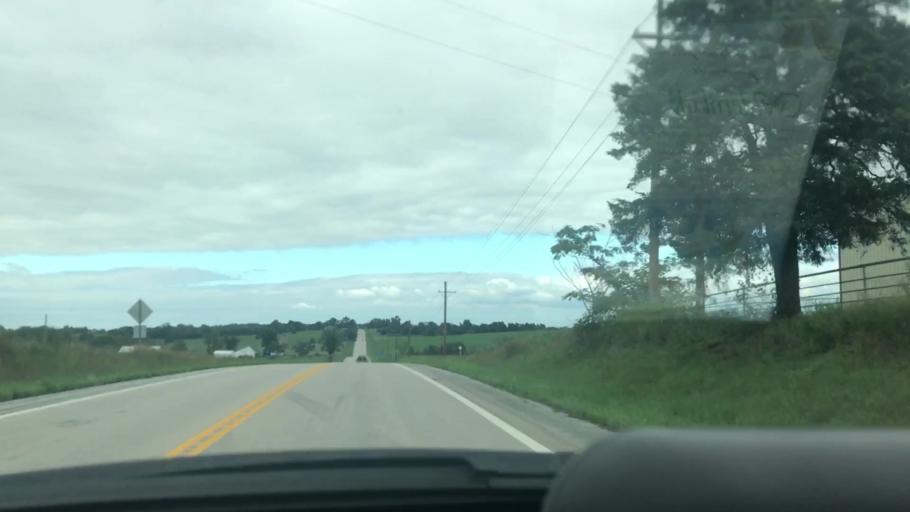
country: US
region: Missouri
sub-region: Hickory County
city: Hermitage
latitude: 37.8843
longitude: -93.1801
